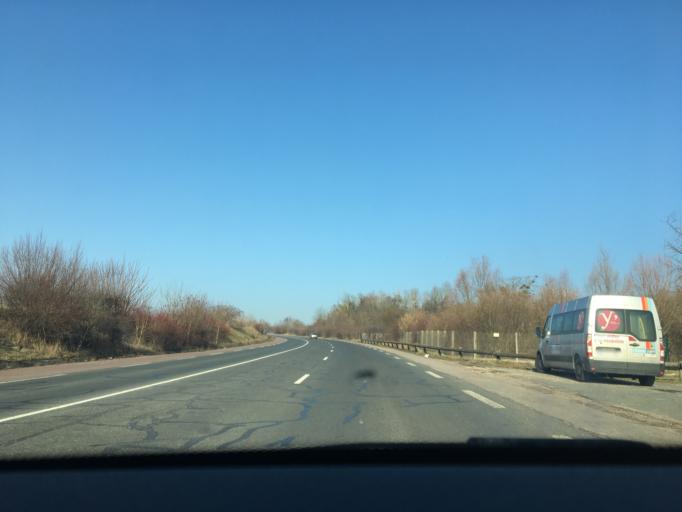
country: FR
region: Ile-de-France
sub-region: Departement des Yvelines
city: Limay
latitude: 48.9982
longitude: 1.7504
